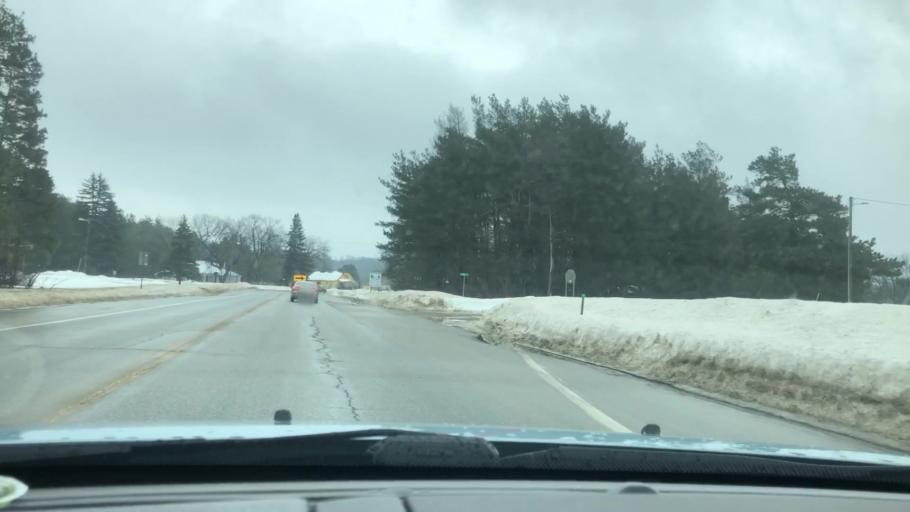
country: US
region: Michigan
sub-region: Otsego County
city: Gaylord
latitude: 45.0662
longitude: -84.8600
